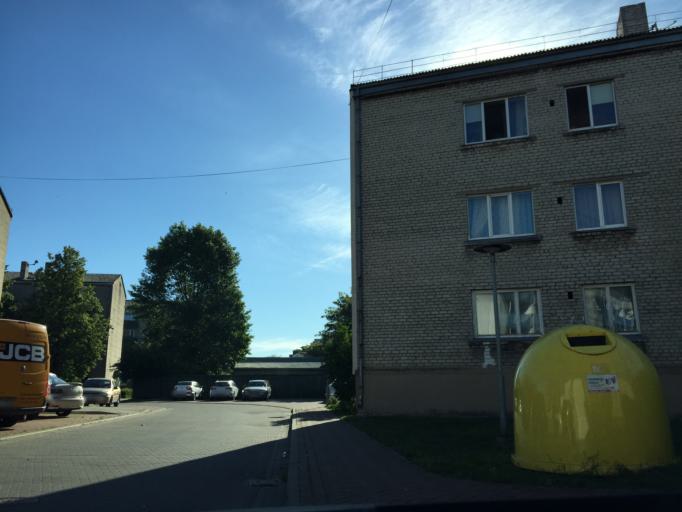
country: LV
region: Ventspils
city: Ventspils
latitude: 57.4028
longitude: 21.5854
